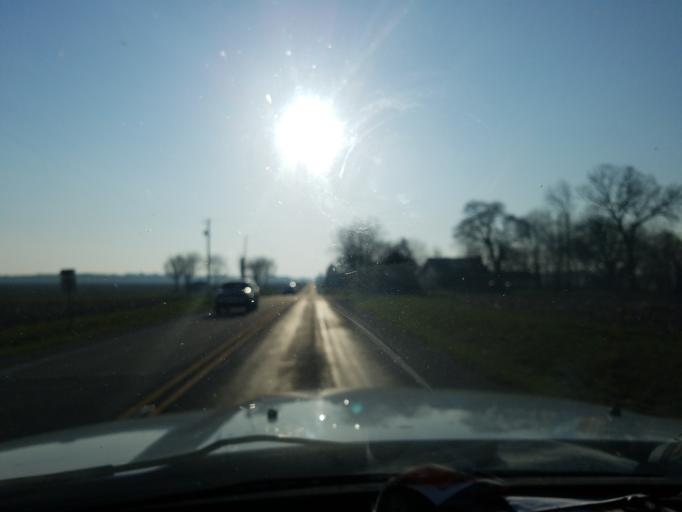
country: US
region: Indiana
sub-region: Vigo County
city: Seelyville
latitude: 39.3891
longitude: -87.2029
